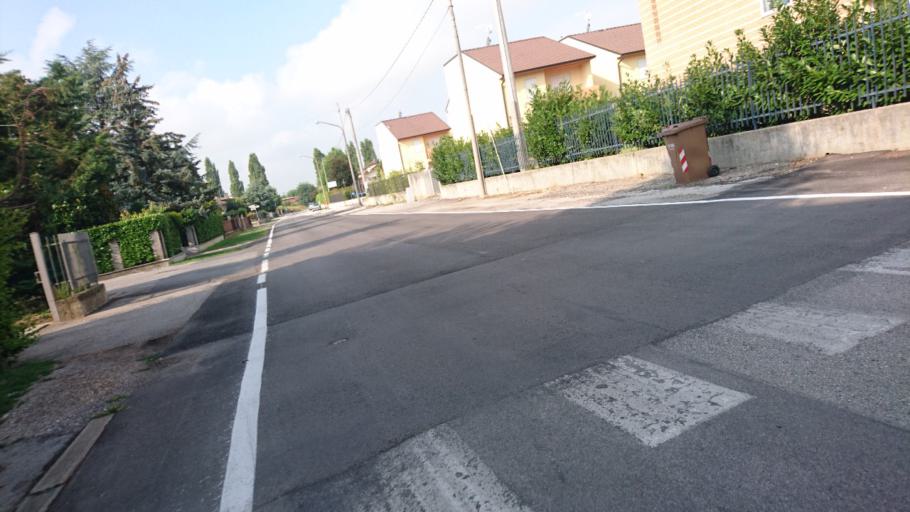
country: IT
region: Veneto
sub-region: Provincia di Vicenza
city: Montegaldella
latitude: 45.4390
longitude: 11.6696
